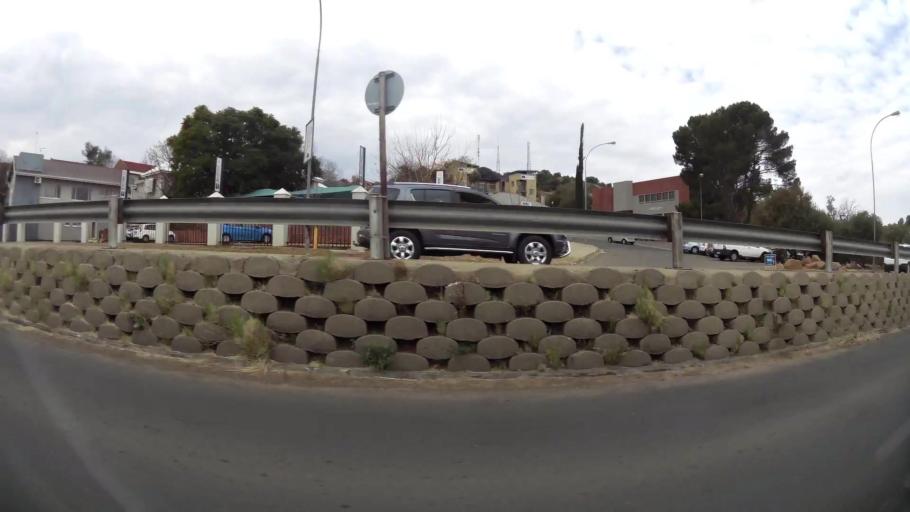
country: ZA
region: Orange Free State
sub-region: Mangaung Metropolitan Municipality
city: Bloemfontein
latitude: -29.1073
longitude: 26.2133
